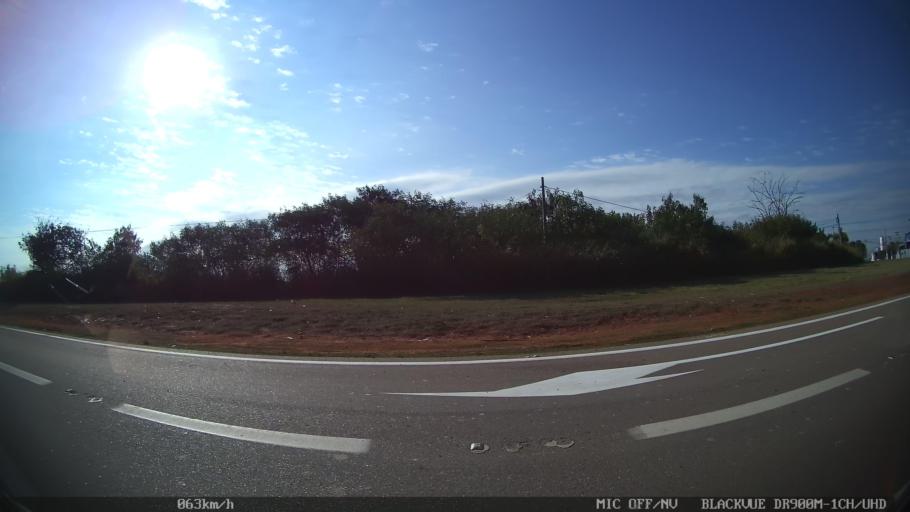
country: BR
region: Sao Paulo
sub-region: Piracicaba
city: Piracicaba
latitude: -22.6618
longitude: -47.6104
